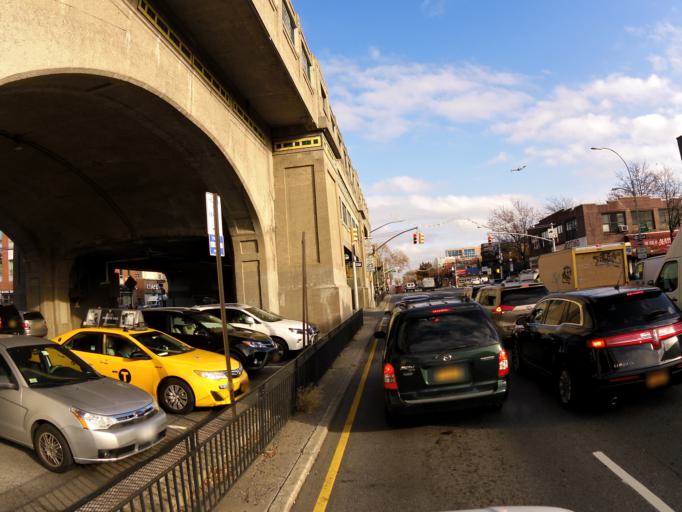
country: US
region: New York
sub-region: Queens County
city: Long Island City
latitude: 40.7430
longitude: -73.9182
